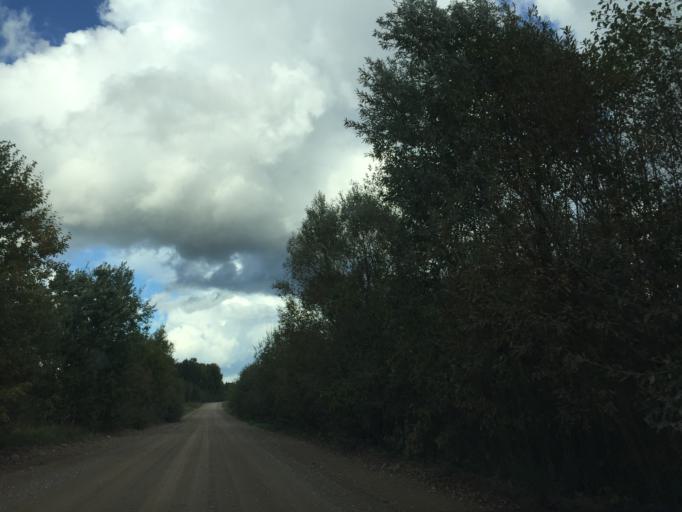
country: LV
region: Malpils
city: Malpils
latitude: 57.0502
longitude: 25.1189
